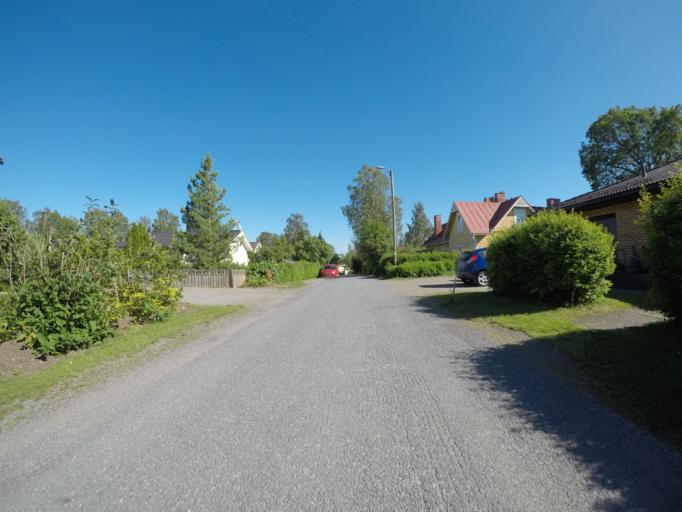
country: FI
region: Haeme
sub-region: Haemeenlinna
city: Haemeenlinna
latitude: 61.0117
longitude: 24.4805
